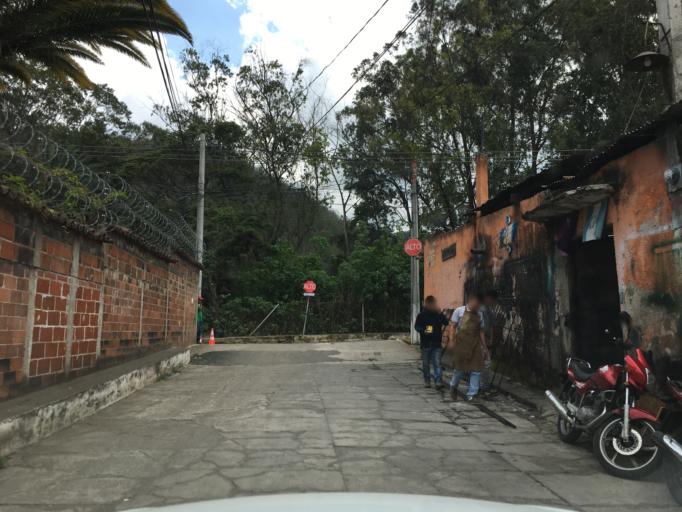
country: GT
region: Sacatepequez
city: Antigua Guatemala
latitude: 14.5632
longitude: -90.7276
